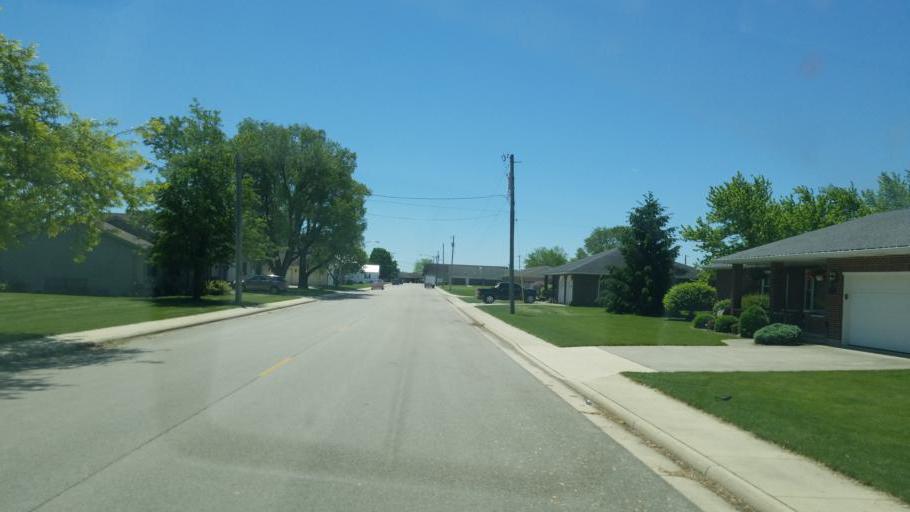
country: US
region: Ohio
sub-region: Mercer County
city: Saint Henry
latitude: 40.3542
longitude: -84.6430
